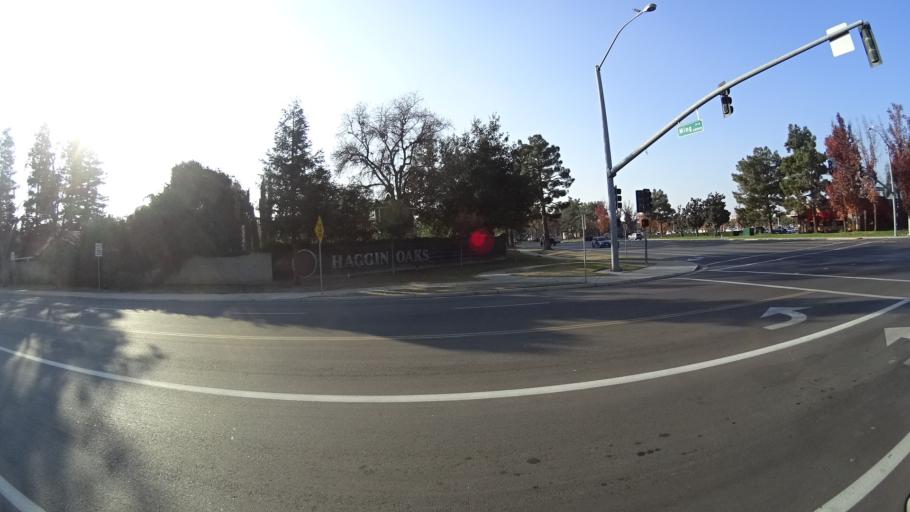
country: US
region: California
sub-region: Kern County
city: Greenacres
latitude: 35.3395
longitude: -119.1010
